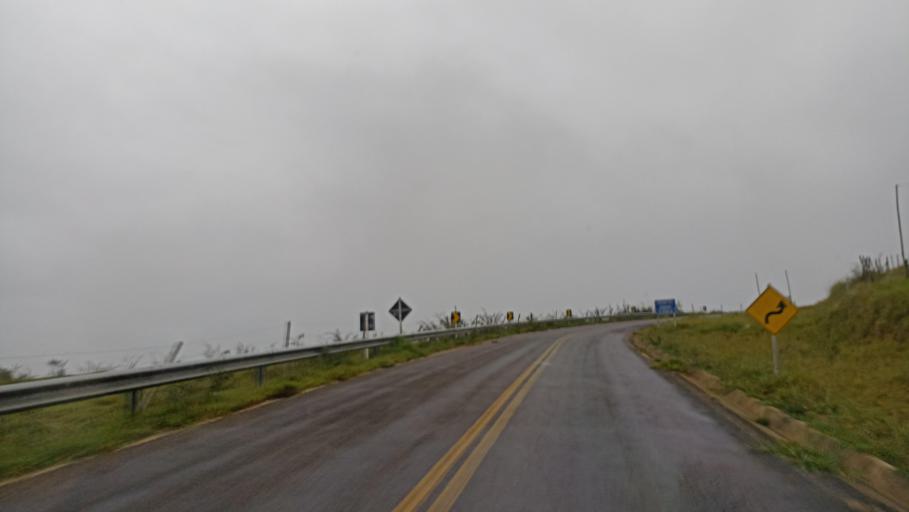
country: BR
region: Bahia
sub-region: Itanhem
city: Itanhem
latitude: -16.7318
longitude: -40.4367
